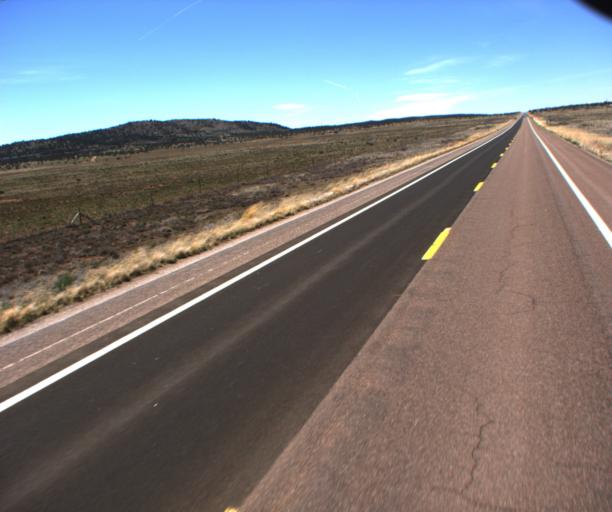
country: US
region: Arizona
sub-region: Mohave County
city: Peach Springs
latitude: 35.4842
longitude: -113.1469
